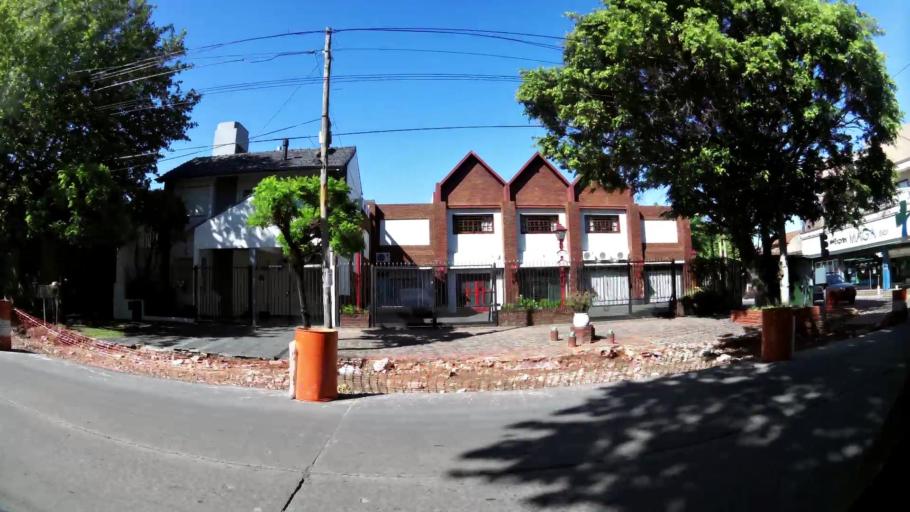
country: AR
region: Buenos Aires
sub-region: Partido de Quilmes
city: Quilmes
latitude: -34.7067
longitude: -58.2875
